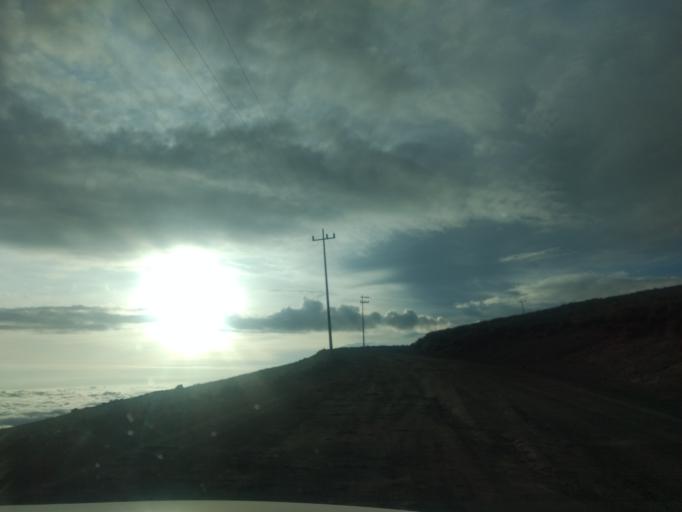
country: MX
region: Mexico
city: Cerro La Calera
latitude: 19.1288
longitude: -99.7645
